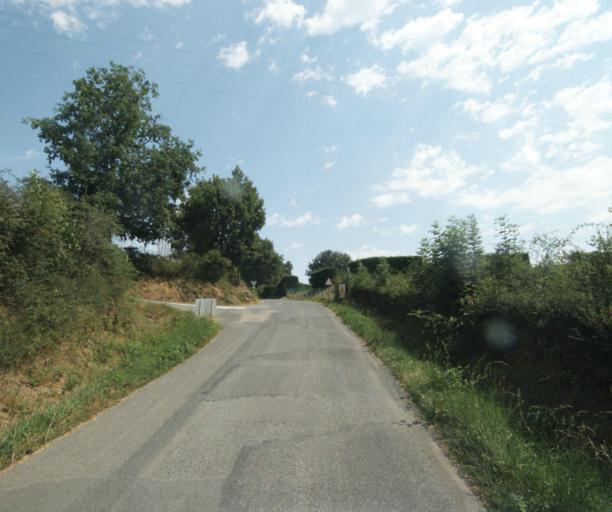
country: FR
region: Rhone-Alpes
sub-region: Departement du Rhone
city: Sourcieux-les-Mines
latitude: 45.8294
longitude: 4.6293
